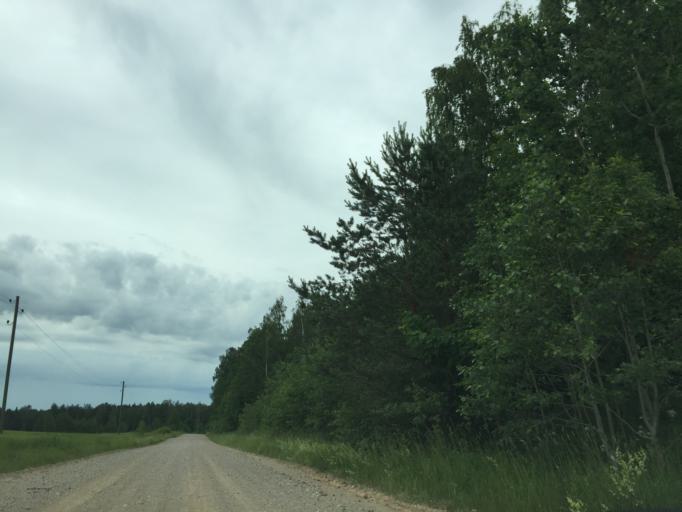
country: LV
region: Tukuma Rajons
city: Tukums
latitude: 57.0410
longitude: 23.0981
